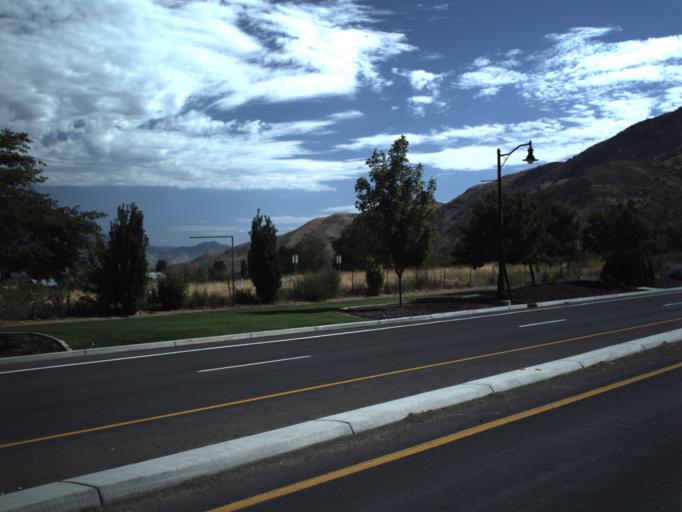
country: US
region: Utah
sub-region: Utah County
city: Santaquin
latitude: 39.9755
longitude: -111.7757
